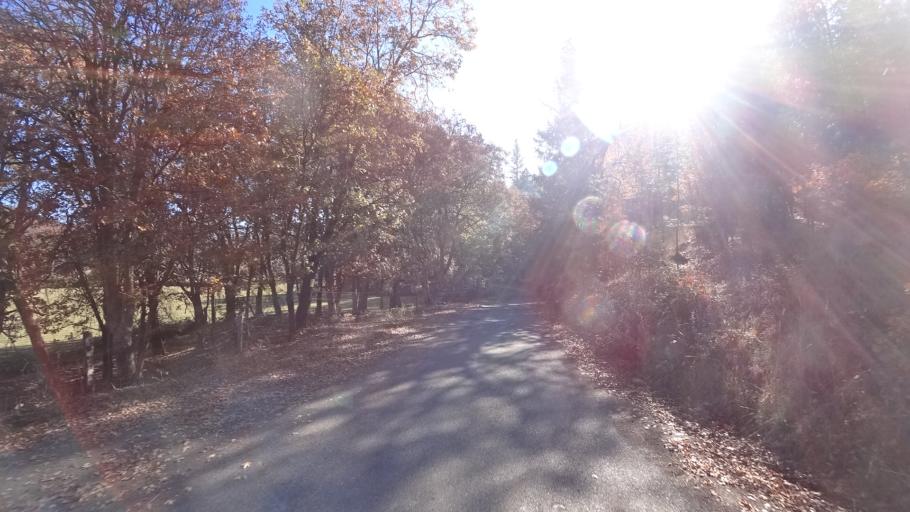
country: US
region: California
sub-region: Siskiyou County
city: Yreka
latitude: 41.8357
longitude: -122.8678
